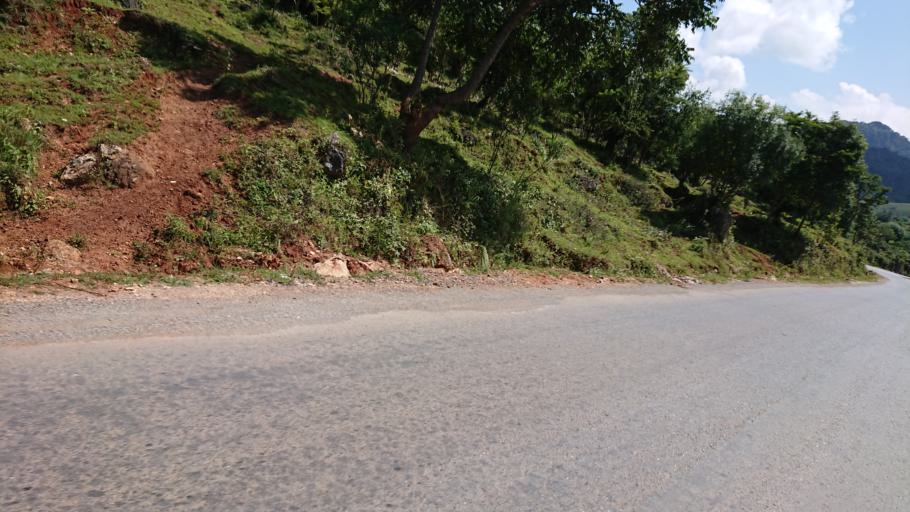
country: MM
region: Shan
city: Taunggyi
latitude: 20.8147
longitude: 97.3298
